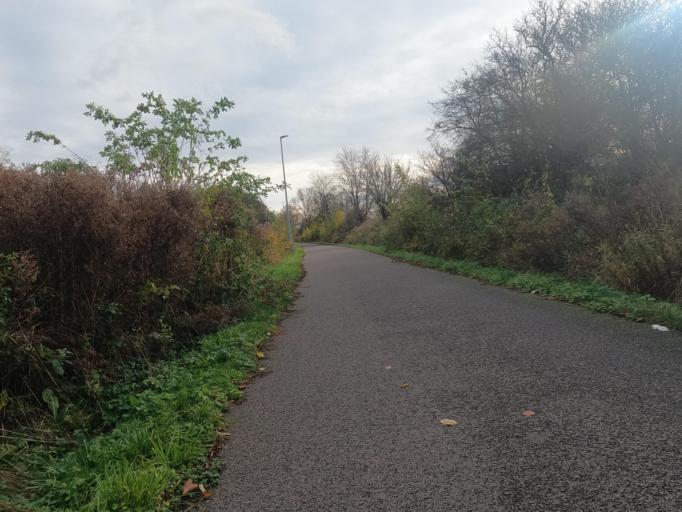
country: PL
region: Pomeranian Voivodeship
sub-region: Powiat starogardzki
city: Starogard Gdanski
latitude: 53.9809
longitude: 18.4762
